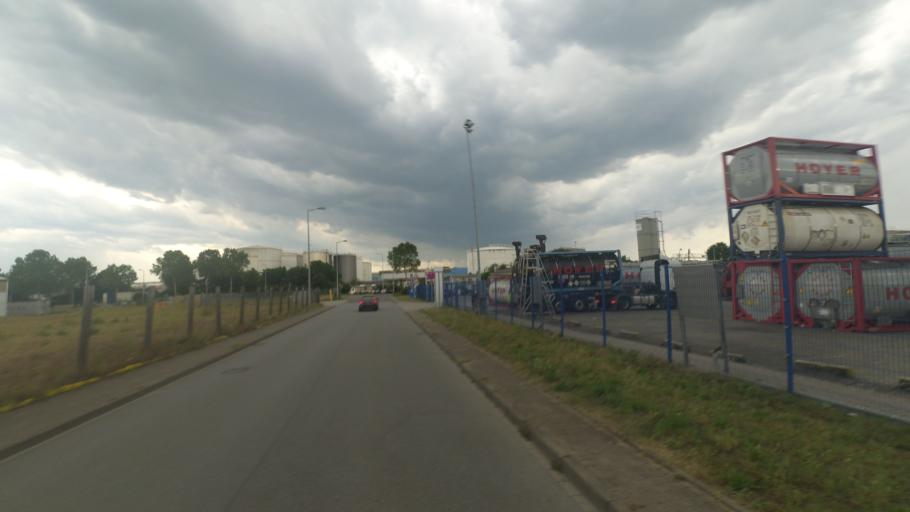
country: DE
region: Rheinland-Pfalz
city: Altrip
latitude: 49.4224
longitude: 8.5078
